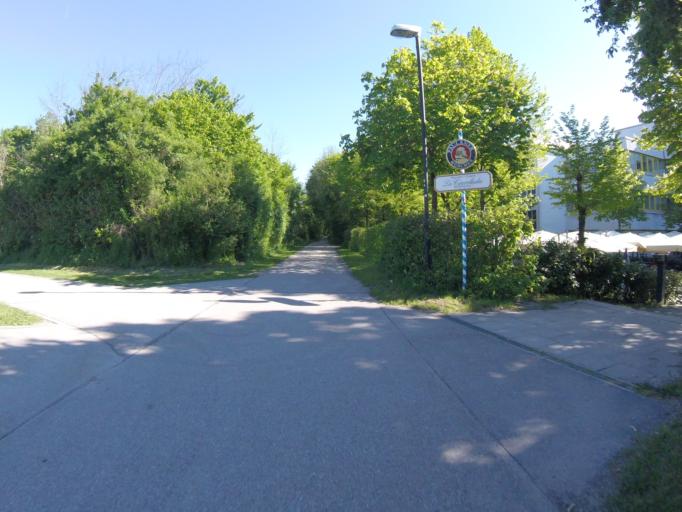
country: DE
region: Bavaria
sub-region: Upper Bavaria
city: Neubiberg
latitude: 48.0758
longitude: 11.6574
